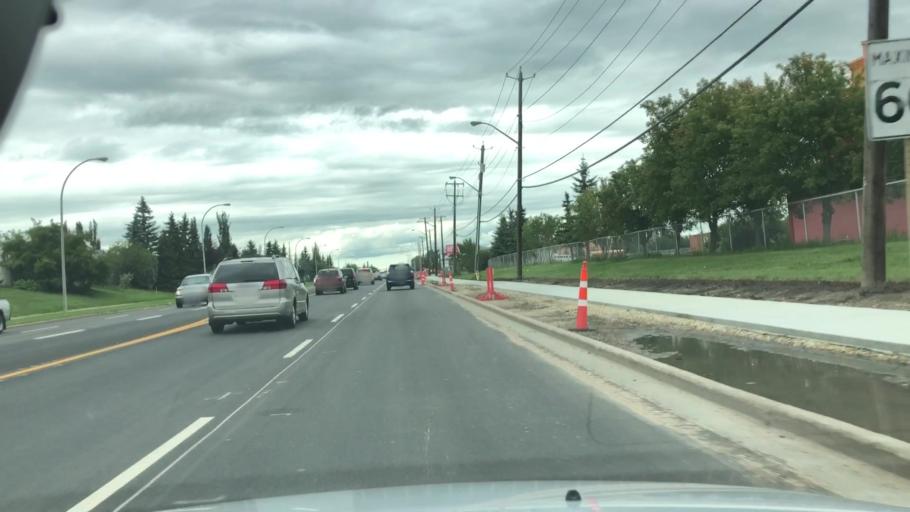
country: CA
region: Alberta
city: Edmonton
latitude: 53.6109
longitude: -113.5412
